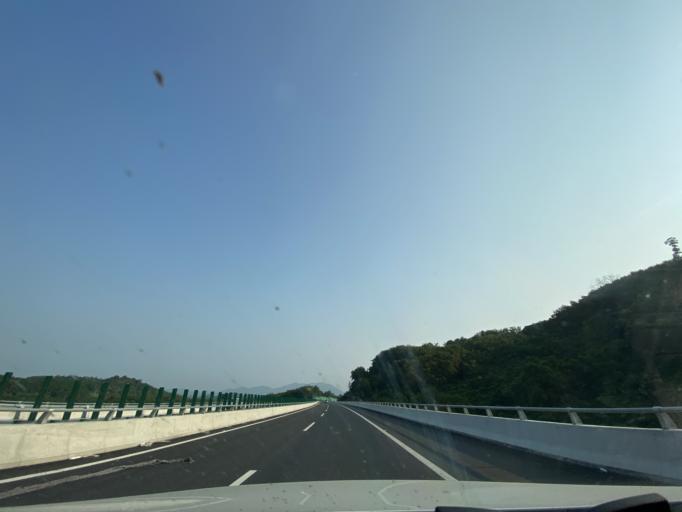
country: CN
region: Hainan
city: Xiangshui
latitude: 18.6523
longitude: 109.6287
